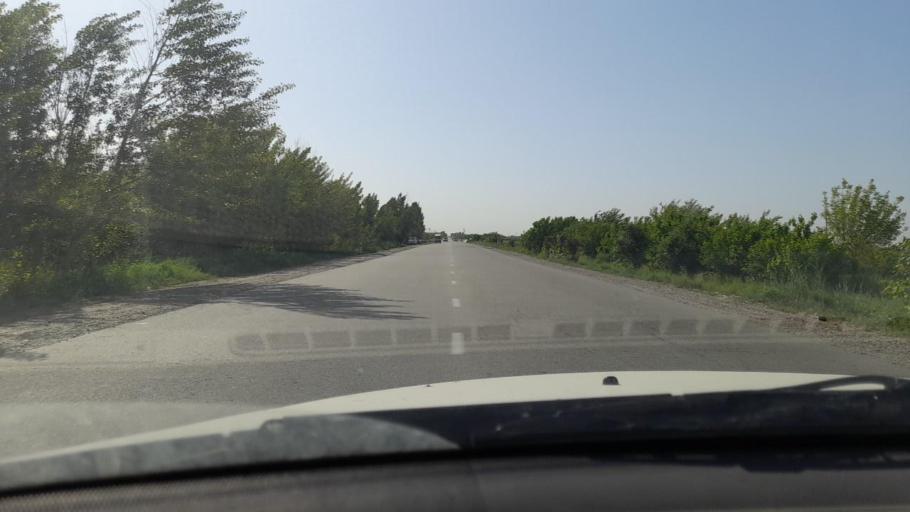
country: UZ
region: Bukhara
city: Romiton
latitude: 39.8961
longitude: 64.4115
